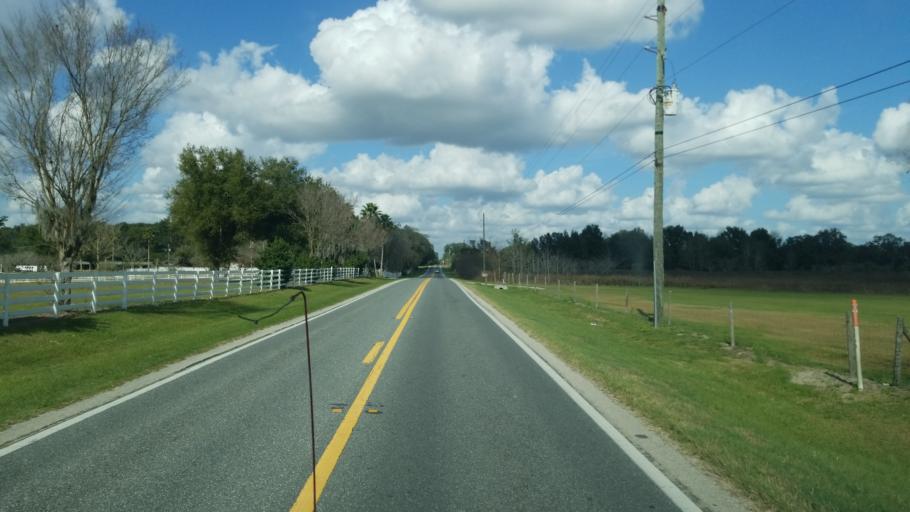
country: US
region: Florida
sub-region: Marion County
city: Belleview
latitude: 28.9898
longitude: -82.1199
